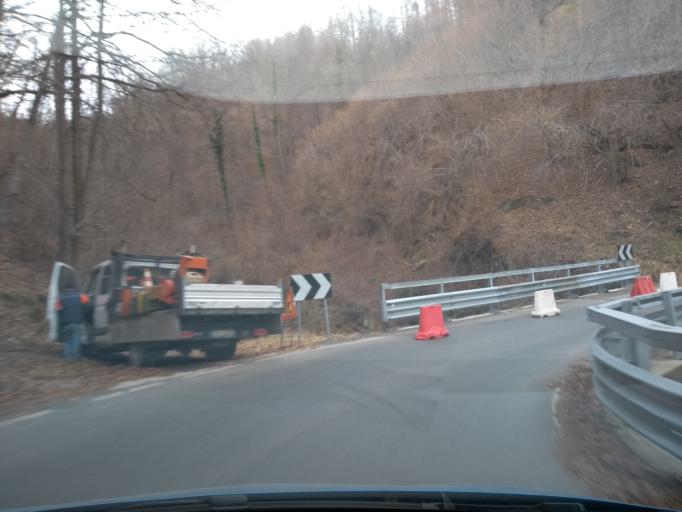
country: IT
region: Piedmont
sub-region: Provincia di Torino
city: Viu
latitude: 45.2389
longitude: 7.3877
